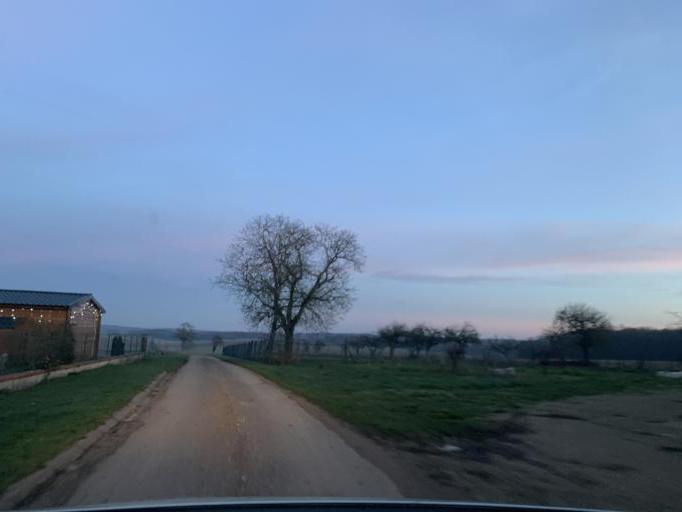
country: FR
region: Bourgogne
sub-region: Departement de l'Yonne
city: Fontenailles
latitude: 47.5620
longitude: 3.3444
